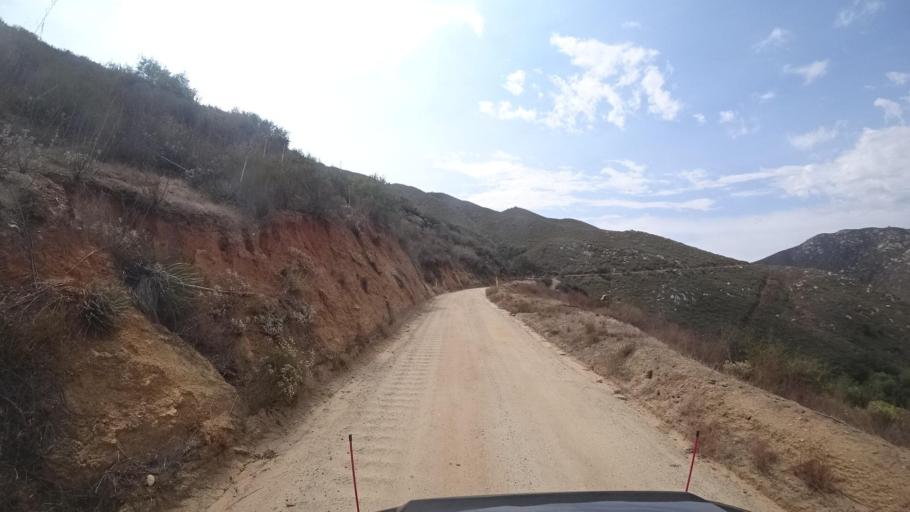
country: US
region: California
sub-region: San Diego County
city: Ramona
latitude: 33.1230
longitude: -116.8055
